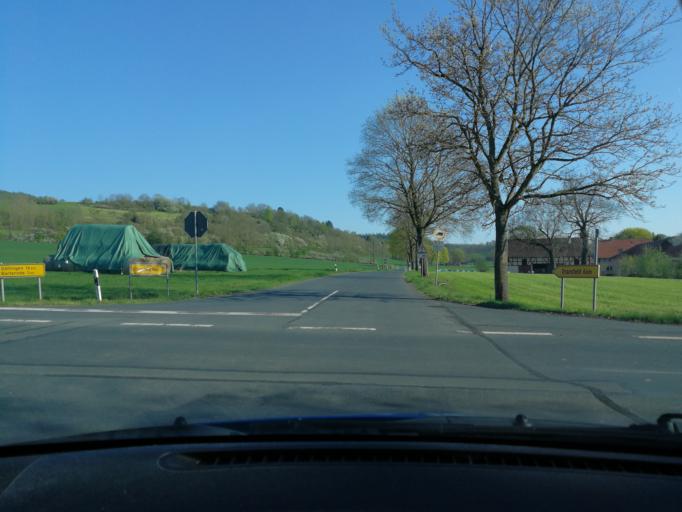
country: DE
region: Lower Saxony
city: Adelebsen
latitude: 51.5441
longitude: 9.7582
